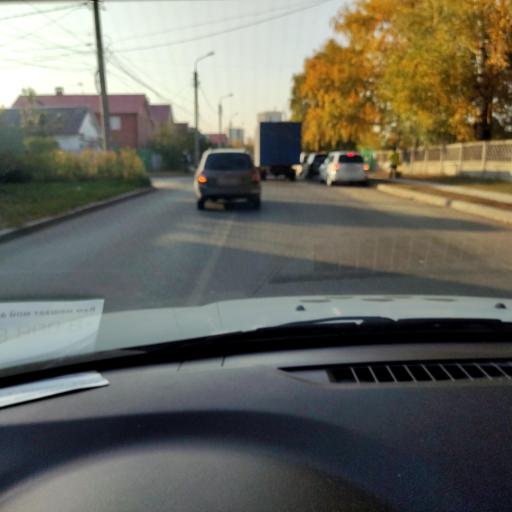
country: RU
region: Samara
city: Tol'yatti
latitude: 53.5265
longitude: 49.4233
